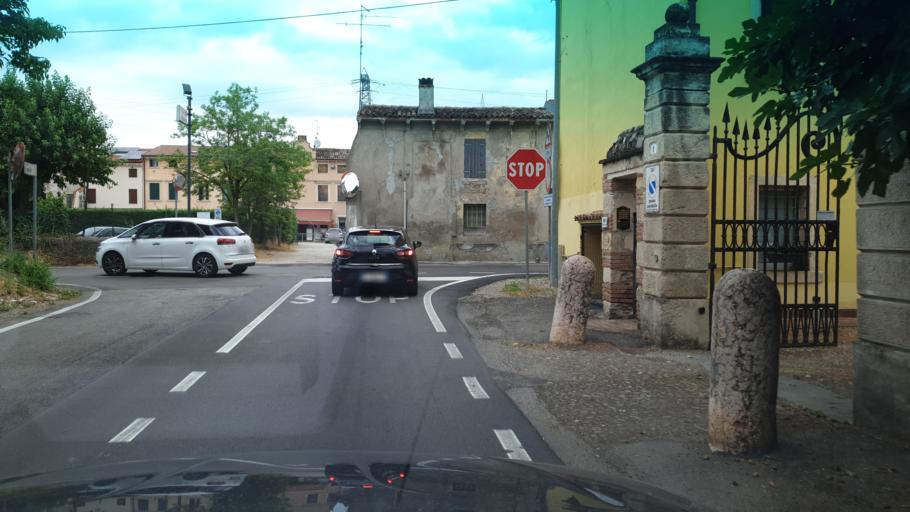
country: IT
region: Veneto
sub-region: Provincia di Verona
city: Beccacivetta-Azzano
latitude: 45.3957
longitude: 10.9734
